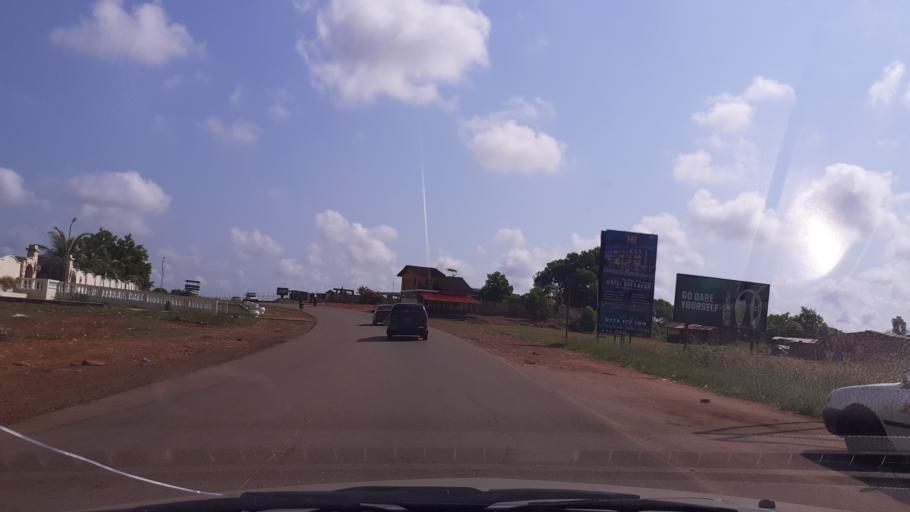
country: LR
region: Montserrado
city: Bensonville City
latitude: 6.2081
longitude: -10.5497
